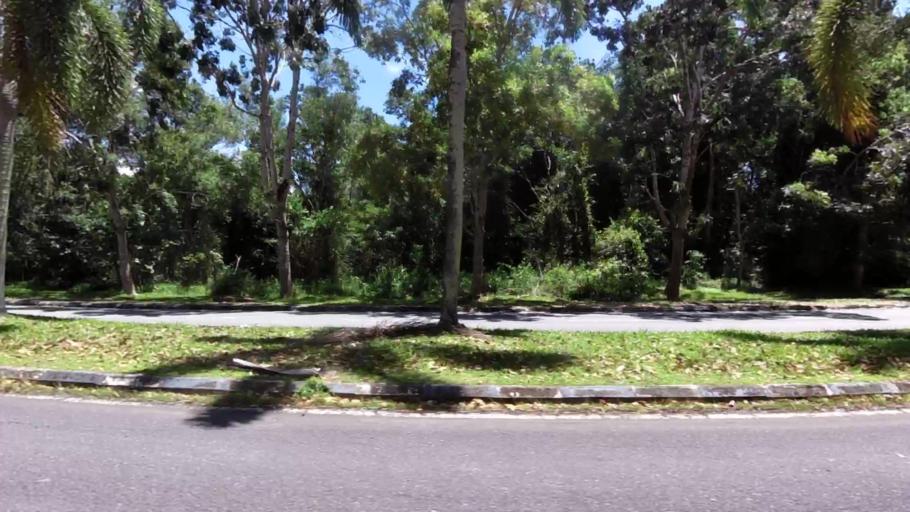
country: BN
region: Brunei and Muara
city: Bandar Seri Begawan
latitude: 4.9222
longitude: 114.9464
